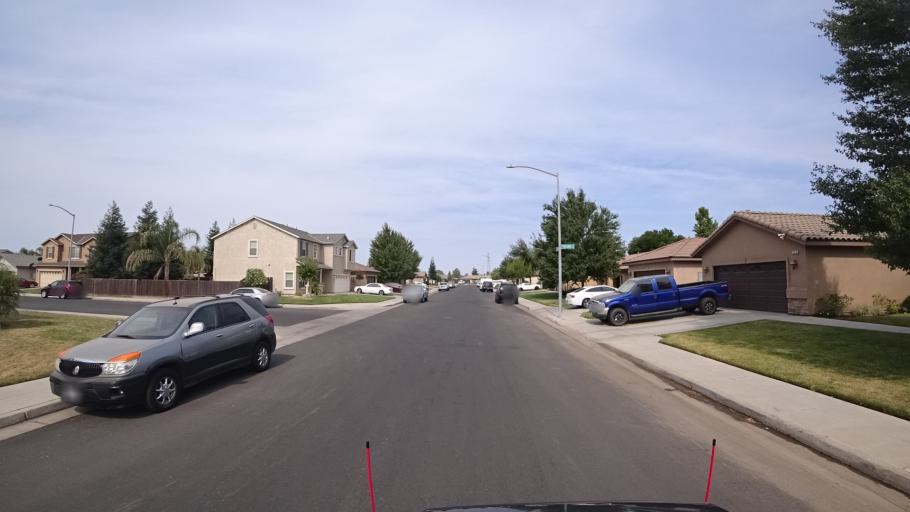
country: US
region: California
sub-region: Fresno County
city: West Park
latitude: 36.7678
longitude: -119.8912
